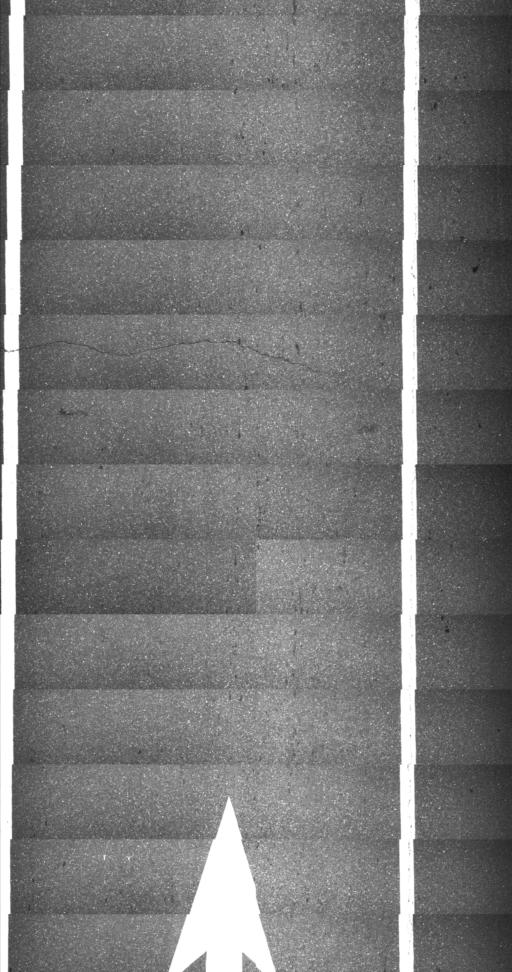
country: US
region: Vermont
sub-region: Windham County
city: Brattleboro
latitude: 42.8454
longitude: -72.5632
